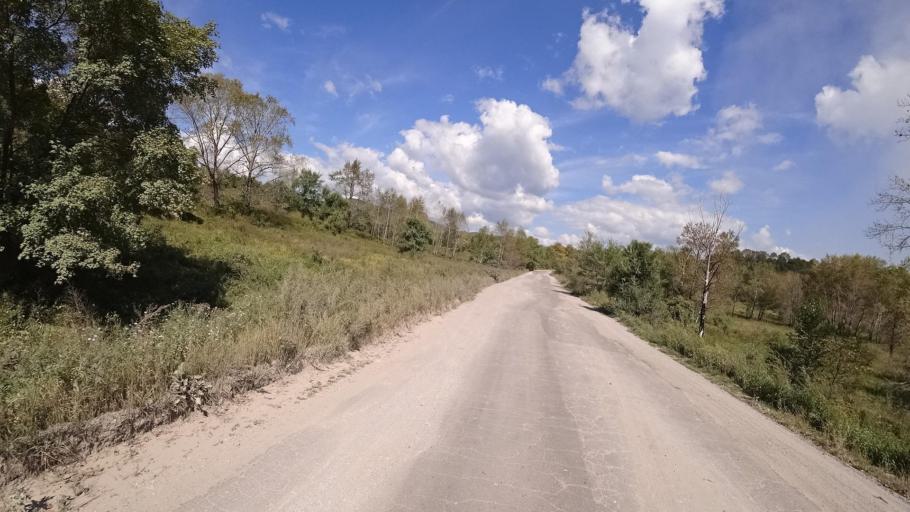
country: RU
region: Jewish Autonomous Oblast
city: Londoko
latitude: 49.0088
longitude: 131.8946
